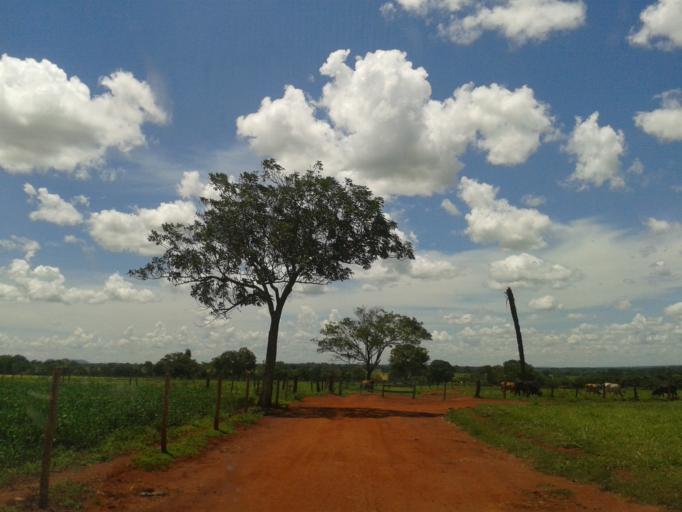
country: BR
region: Minas Gerais
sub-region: Capinopolis
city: Capinopolis
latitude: -18.7759
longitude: -49.8046
